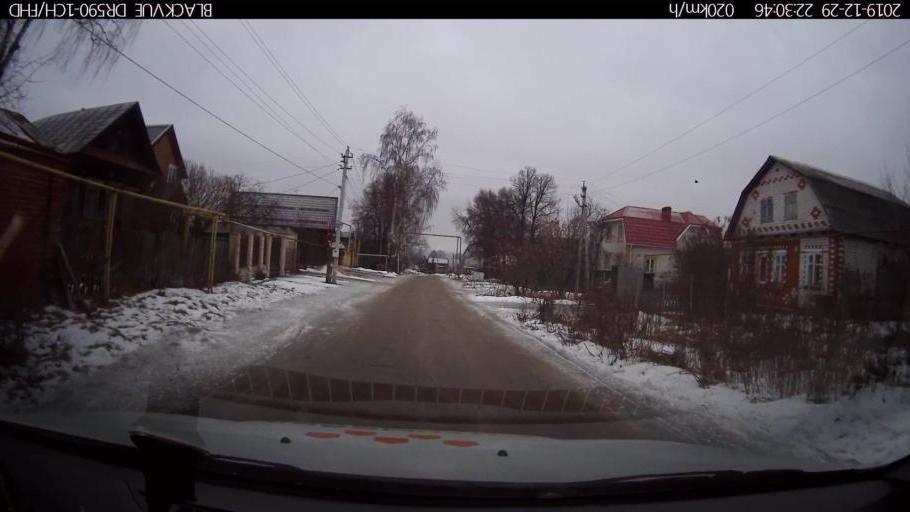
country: RU
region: Nizjnij Novgorod
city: Afonino
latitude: 56.2049
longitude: 43.9862
